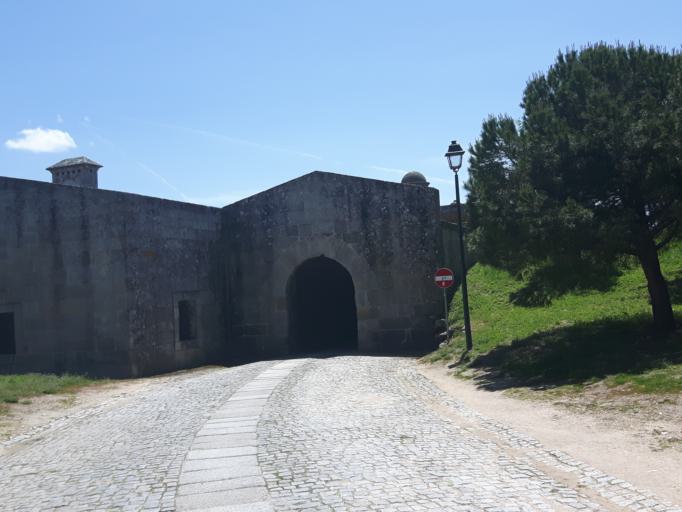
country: ES
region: Castille and Leon
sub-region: Provincia de Salamanca
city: Aldea del Obispo
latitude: 40.7237
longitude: -6.9045
